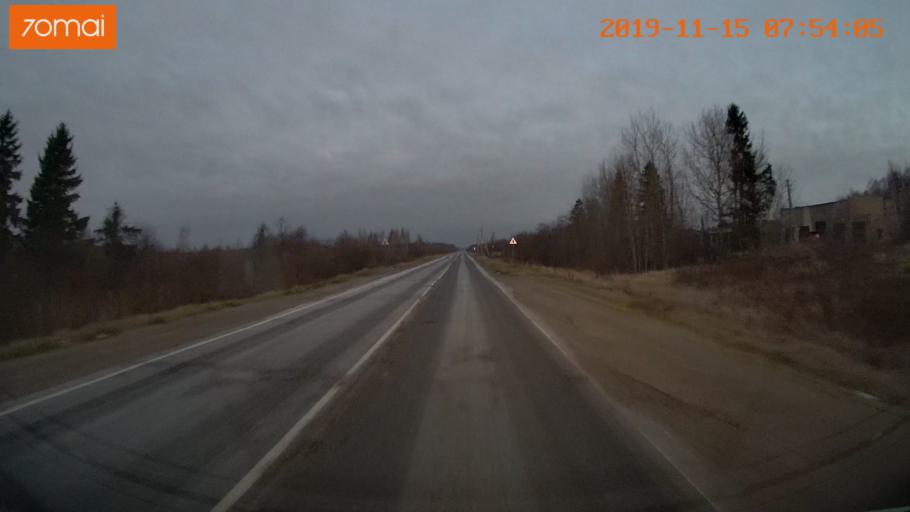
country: RU
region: Vologda
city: Cherepovets
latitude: 58.8953
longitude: 38.1798
